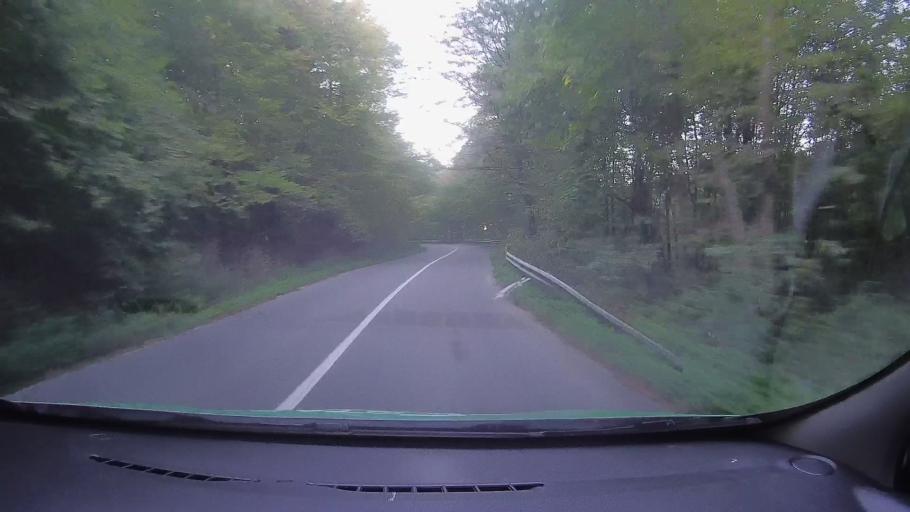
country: RO
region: Timis
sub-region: Comuna Fardea
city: Fardea
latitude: 45.7490
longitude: 22.1307
